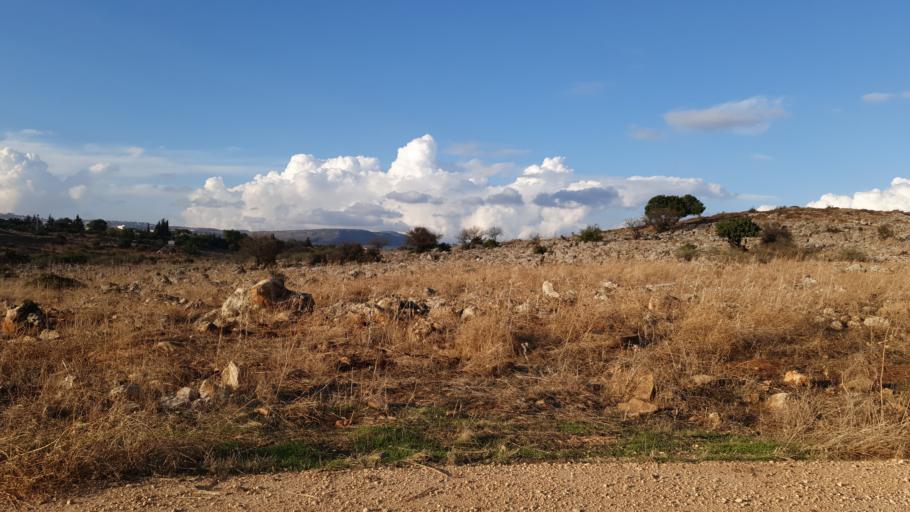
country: IL
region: Northern District
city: Qiryat Shemona
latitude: 33.0919
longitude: 35.5565
